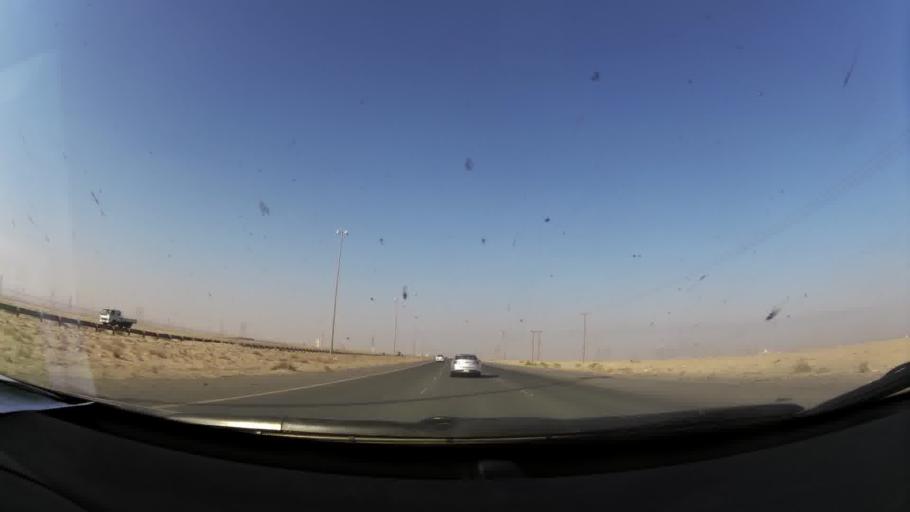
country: IQ
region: Basra Governorate
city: Umm Qasr
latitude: 29.8164
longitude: 47.6746
